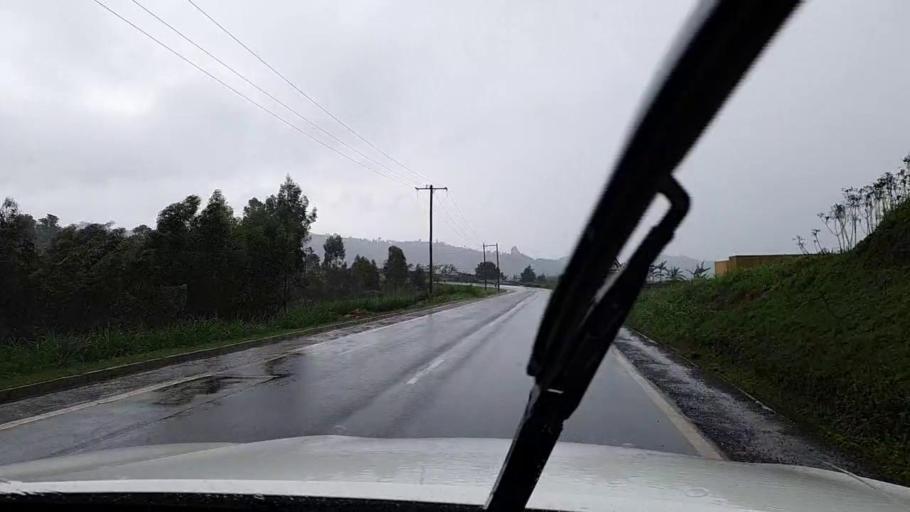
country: RW
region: Western Province
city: Cyangugu
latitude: -2.4619
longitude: 28.9893
